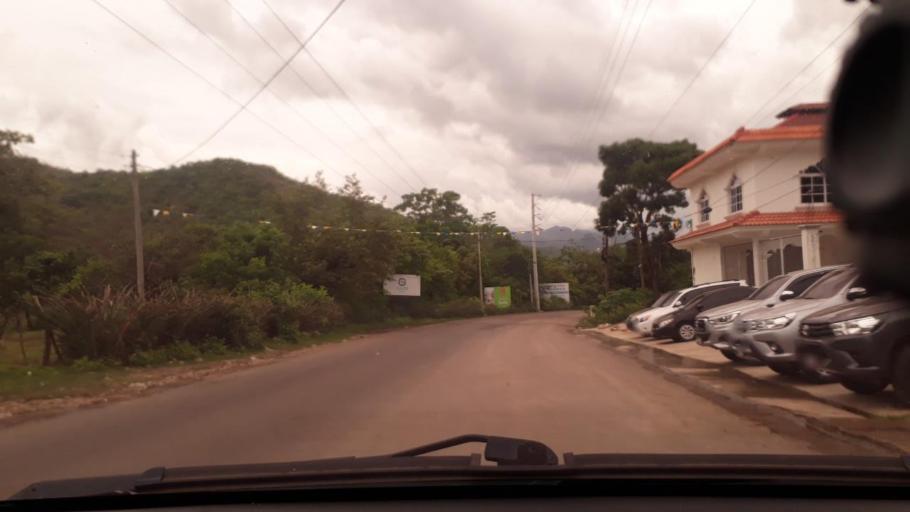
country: GT
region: Chiquimula
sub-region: Municipio de Jocotan
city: Jocotan
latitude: 14.8042
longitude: -89.3922
